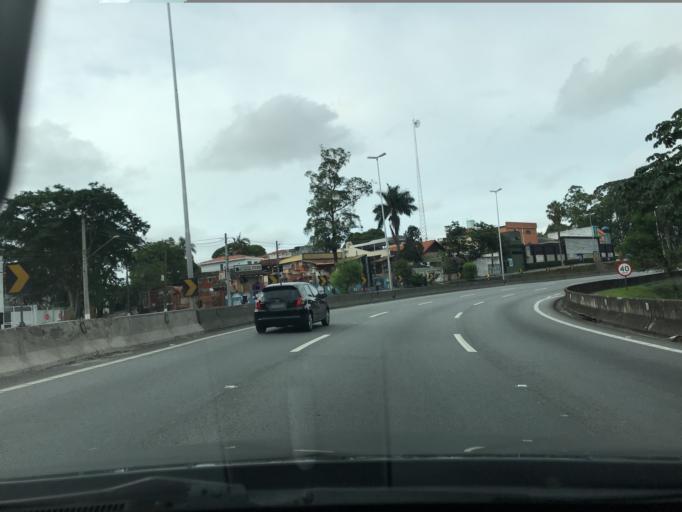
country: BR
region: Sao Paulo
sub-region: Taboao Da Serra
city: Taboao da Serra
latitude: -23.5802
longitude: -46.7288
